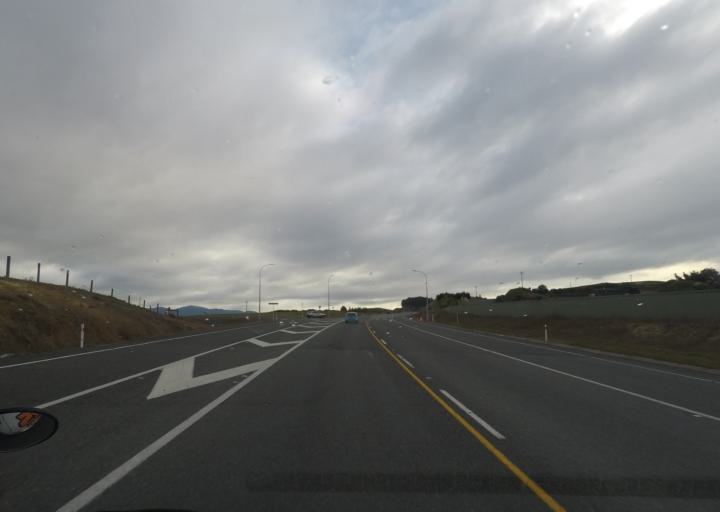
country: NZ
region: Tasman
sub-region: Tasman District
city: Mapua
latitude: -41.2453
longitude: 173.0563
